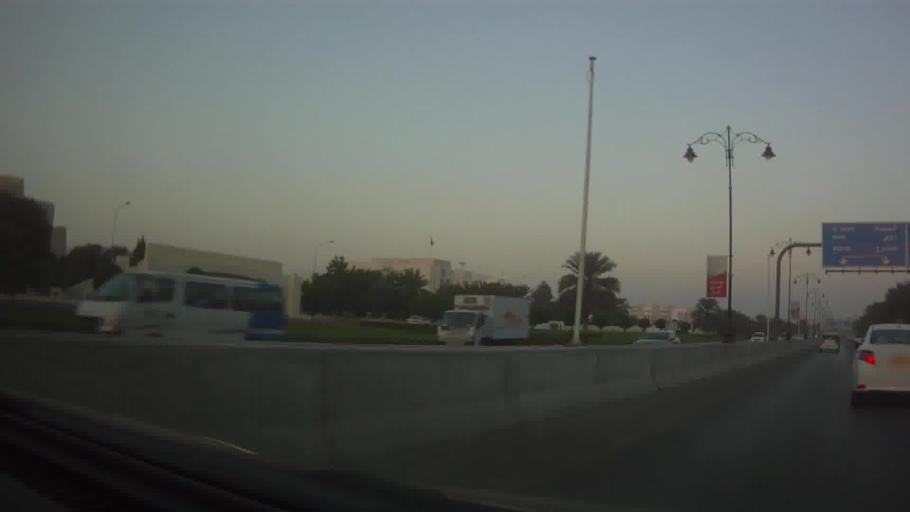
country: OM
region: Muhafazat Masqat
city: Bawshar
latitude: 23.5971
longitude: 58.4288
